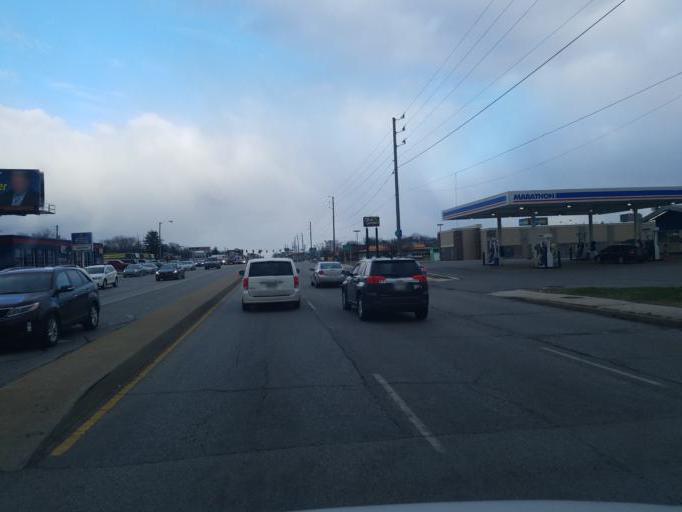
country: US
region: Indiana
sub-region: Marion County
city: Warren Park
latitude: 39.7730
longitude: -86.0262
